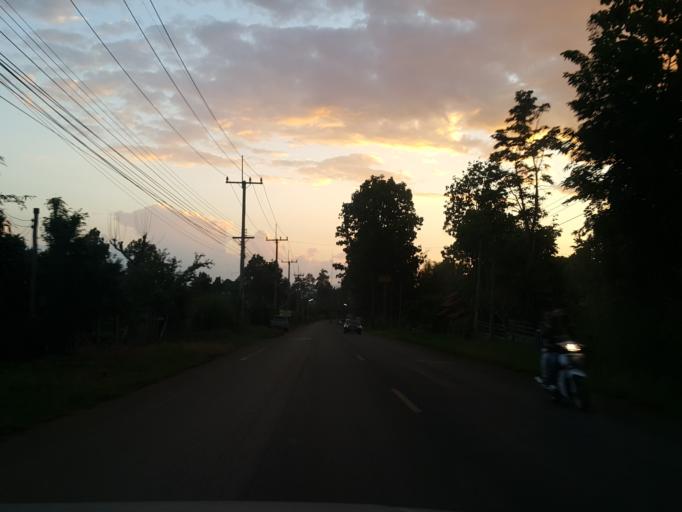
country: TH
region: Mae Hong Son
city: Khun Yuam
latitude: 18.8434
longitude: 97.9558
